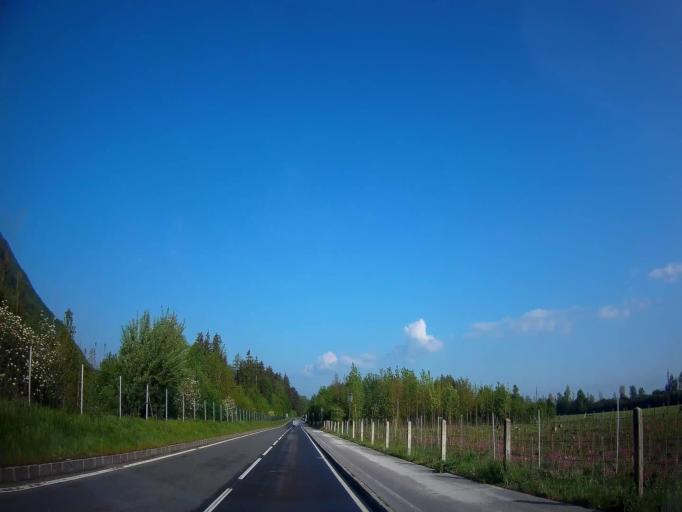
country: AT
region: Salzburg
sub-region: Politischer Bezirk Salzburg-Umgebung
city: Grodig
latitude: 47.7450
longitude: 13.0263
